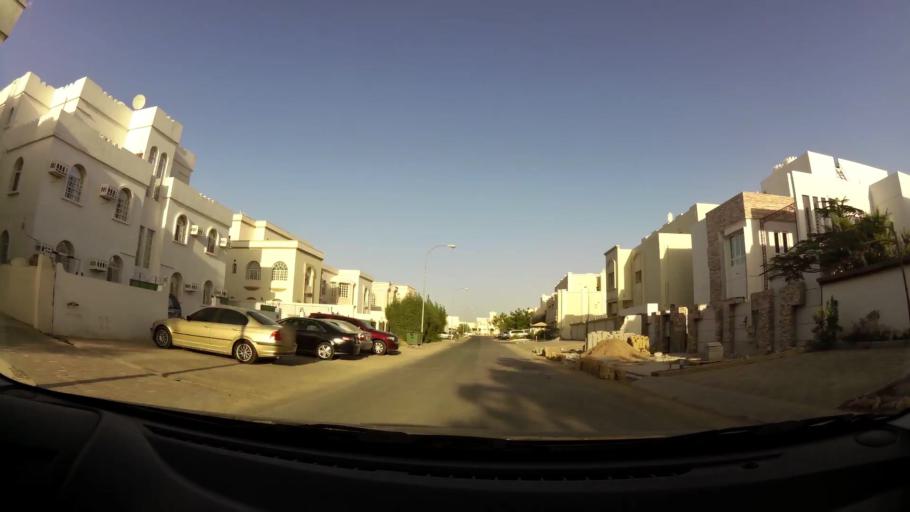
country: OM
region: Muhafazat Masqat
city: As Sib al Jadidah
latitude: 23.6111
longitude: 58.2354
